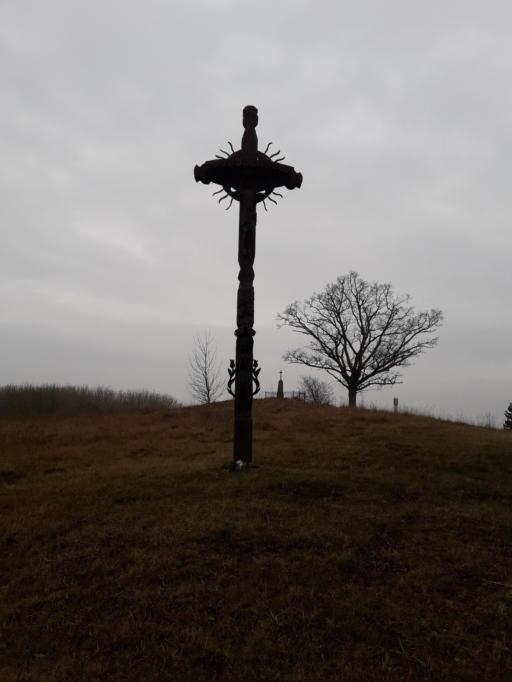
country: LT
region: Alytaus apskritis
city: Druskininkai
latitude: 54.1467
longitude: 24.0831
